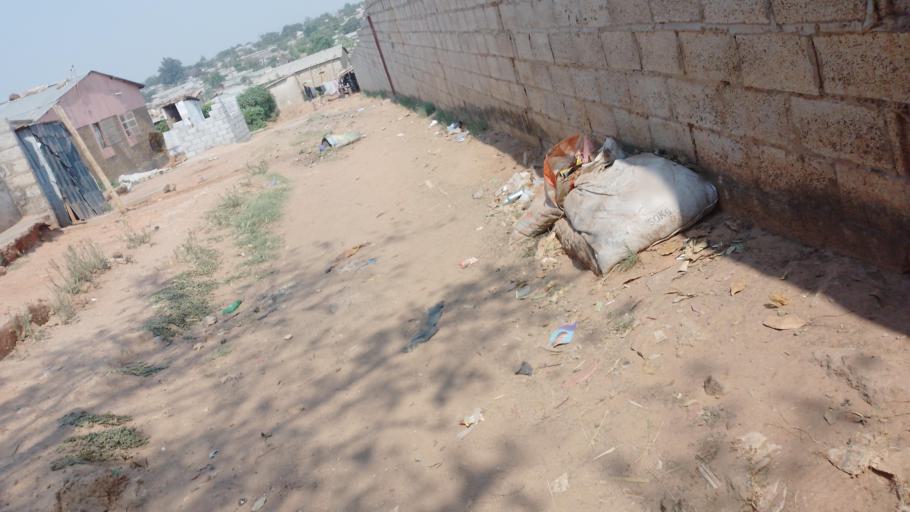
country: ZM
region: Lusaka
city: Lusaka
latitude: -15.4007
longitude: 28.3665
